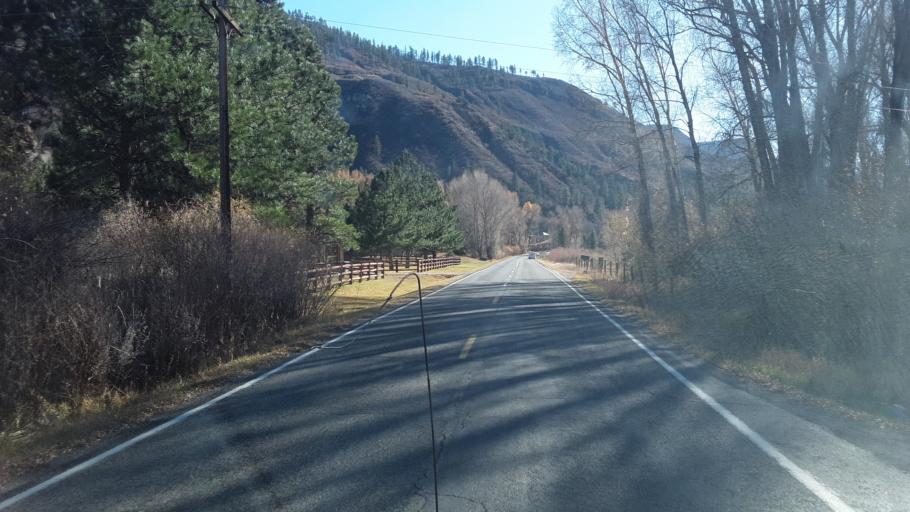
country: US
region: Colorado
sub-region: La Plata County
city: Durango
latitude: 37.4242
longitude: -107.7996
